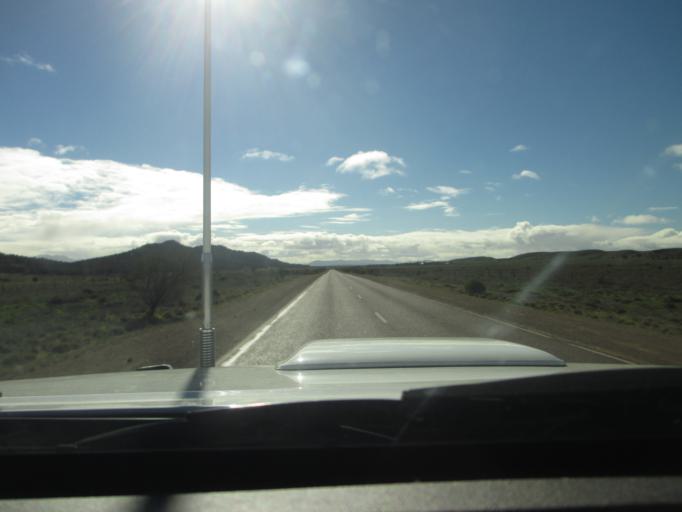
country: AU
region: South Australia
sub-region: Flinders Ranges
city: Quorn
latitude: -31.9477
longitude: 138.3981
